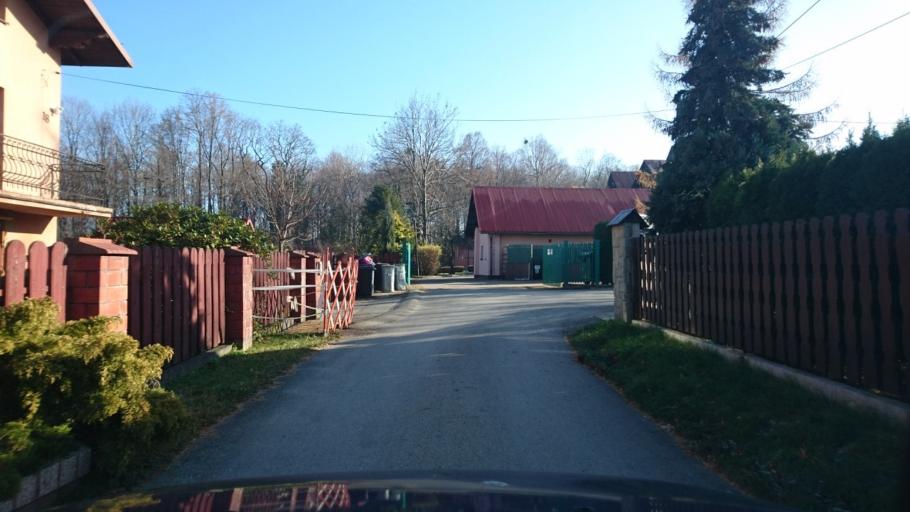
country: PL
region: Silesian Voivodeship
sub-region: Bielsko-Biala
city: Bielsko-Biala
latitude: 49.7911
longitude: 19.0287
